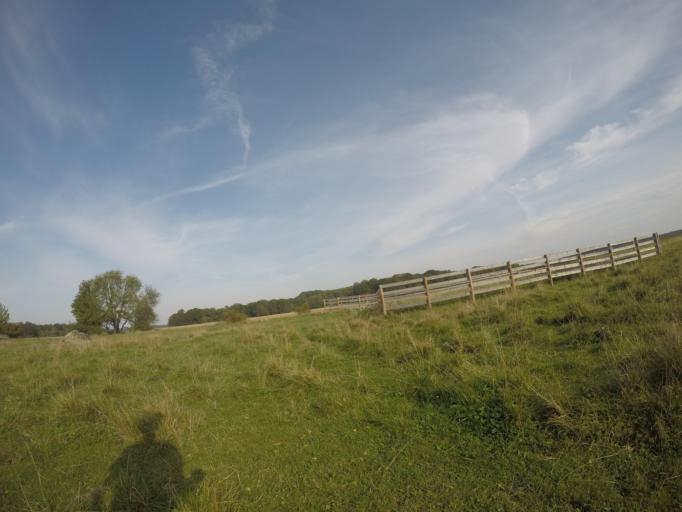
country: SE
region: Vaestmanland
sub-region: Hallstahammars Kommun
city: Kolback
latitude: 59.4780
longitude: 16.2169
